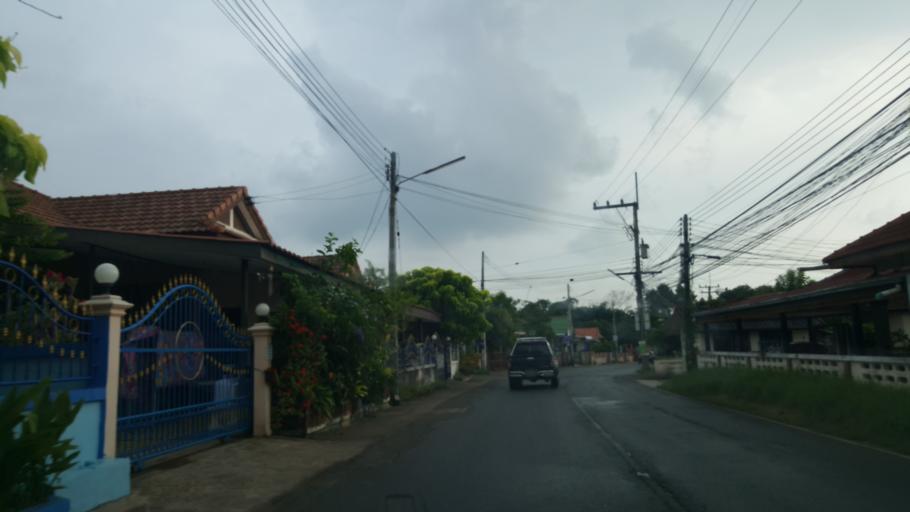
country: TH
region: Chon Buri
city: Sattahip
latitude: 12.6925
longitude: 100.9082
